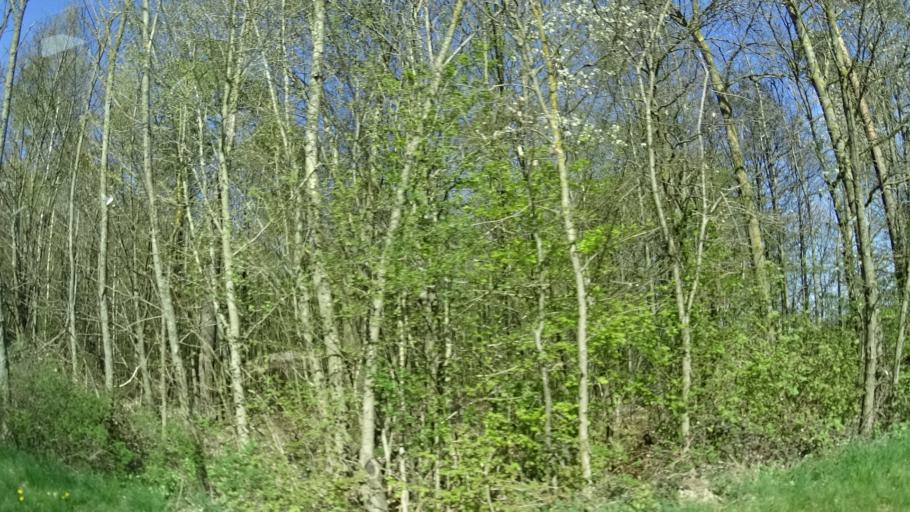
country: DE
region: Bavaria
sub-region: Upper Palatinate
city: Edelsfeld
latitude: 49.5464
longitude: 11.7163
